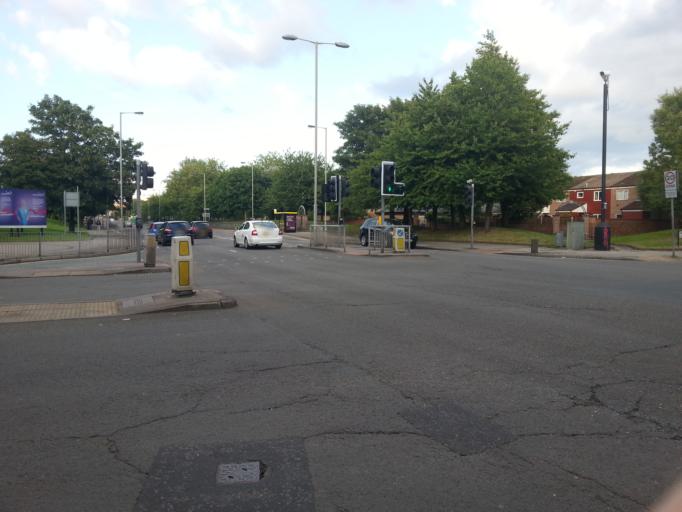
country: GB
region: England
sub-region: Liverpool
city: Liverpool
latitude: 53.3971
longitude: -2.9615
